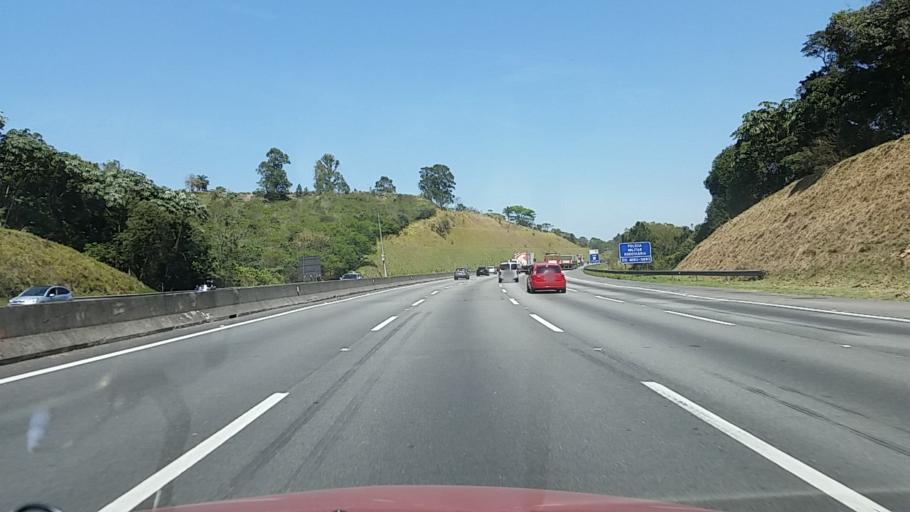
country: BR
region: Sao Paulo
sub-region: Taboao Da Serra
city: Taboao da Serra
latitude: -23.6078
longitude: -46.8146
